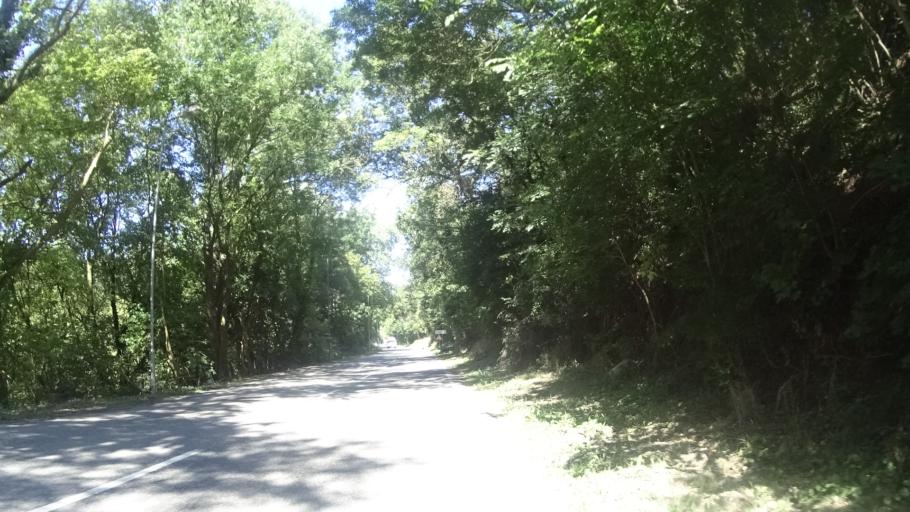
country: AT
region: Lower Austria
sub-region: Politischer Bezirk Bruck an der Leitha
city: Wolfsthal
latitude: 48.1496
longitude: 17.0417
